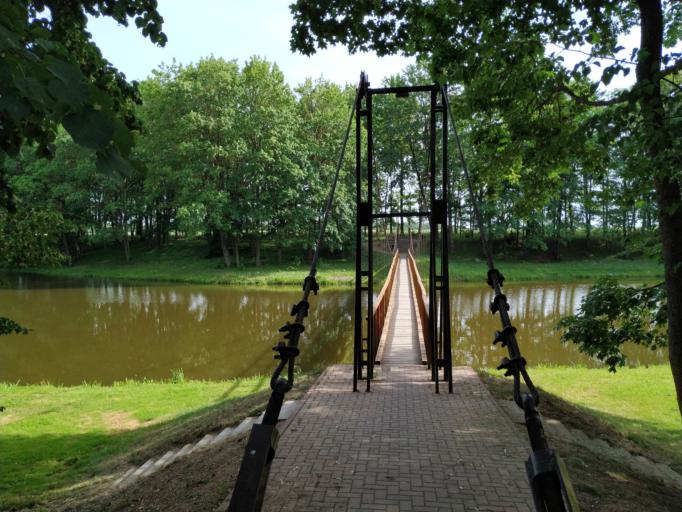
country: LT
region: Panevezys
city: Pasvalys
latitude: 56.1075
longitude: 24.4917
